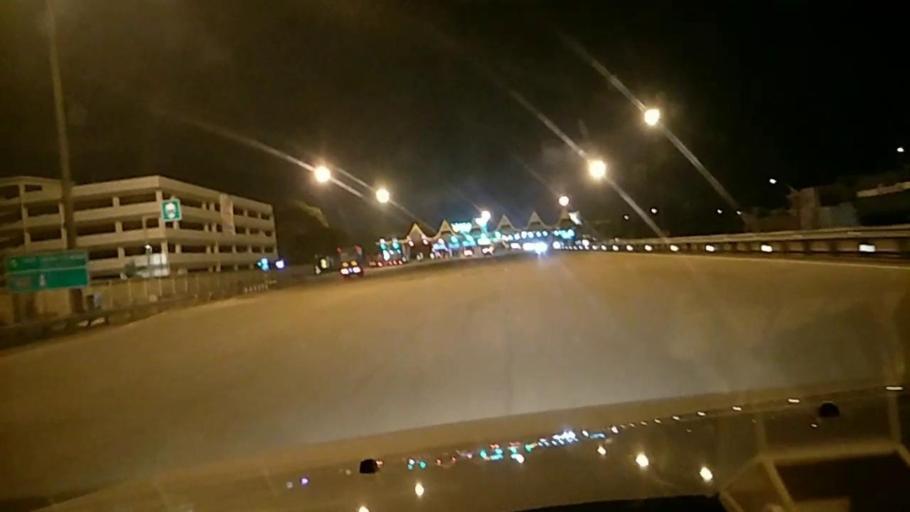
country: MY
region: Penang
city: Juru
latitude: 5.3215
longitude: 100.4369
